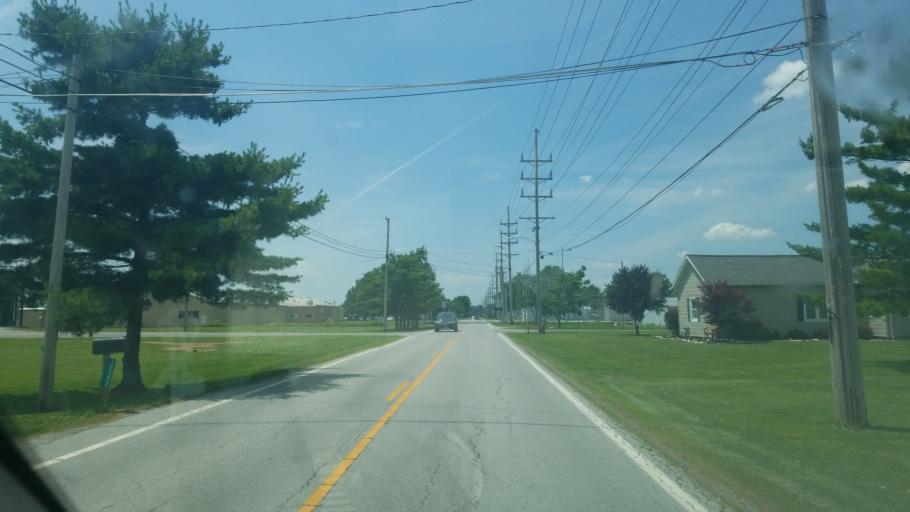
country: US
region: Ohio
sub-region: Hancock County
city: Arlington
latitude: 40.7830
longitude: -83.6443
